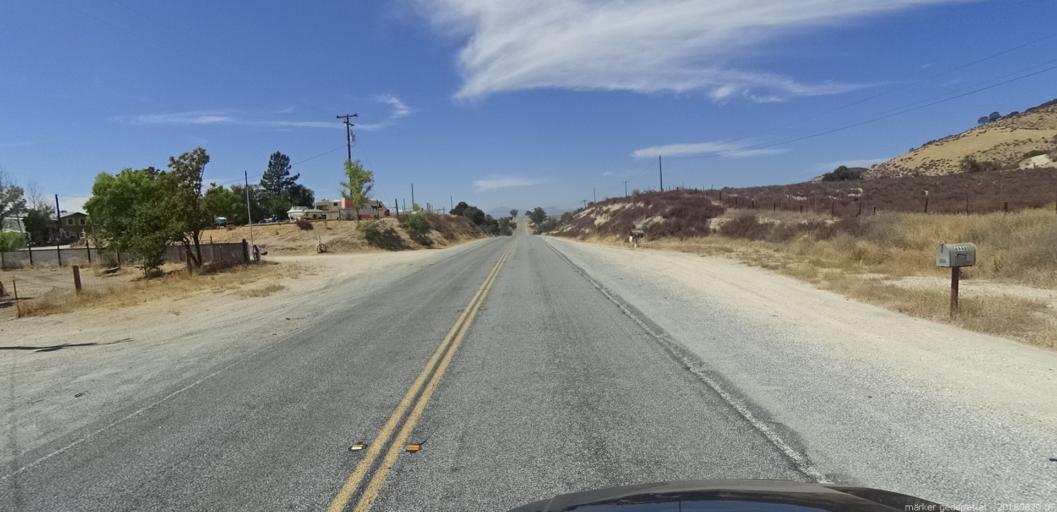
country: US
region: California
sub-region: San Luis Obispo County
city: Lake Nacimiento
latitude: 35.9156
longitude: -121.0268
